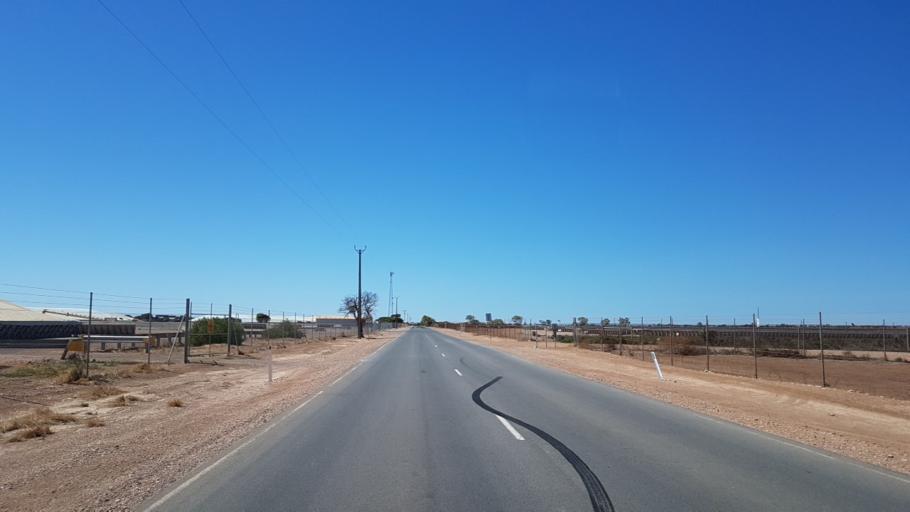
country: AU
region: South Australia
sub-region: Copper Coast
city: Wallaroo
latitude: -33.9378
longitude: 137.6096
